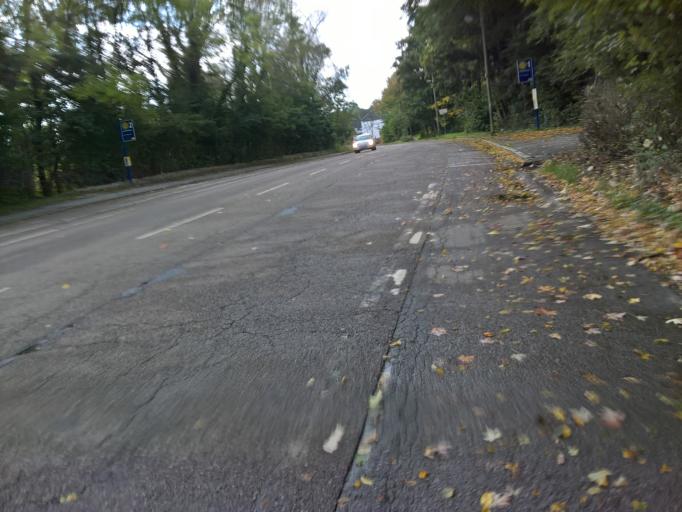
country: DE
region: North Rhine-Westphalia
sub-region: Regierungsbezirk Dusseldorf
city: Velbert
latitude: 51.4008
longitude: 7.0756
